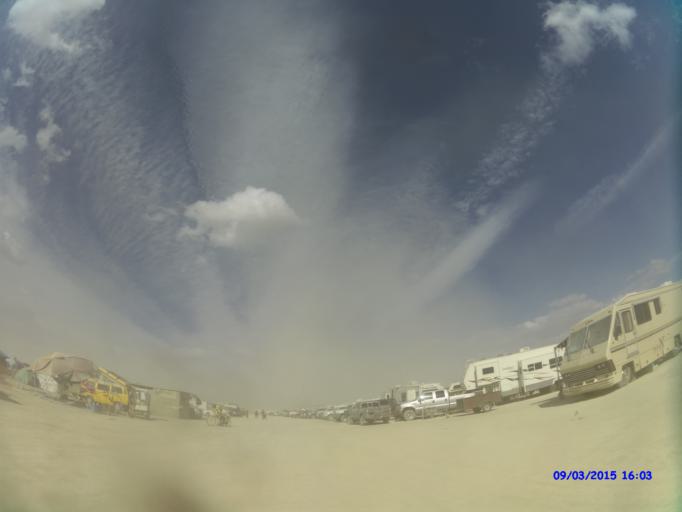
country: US
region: Nevada
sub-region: Pershing County
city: Lovelock
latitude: 40.7790
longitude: -119.1988
